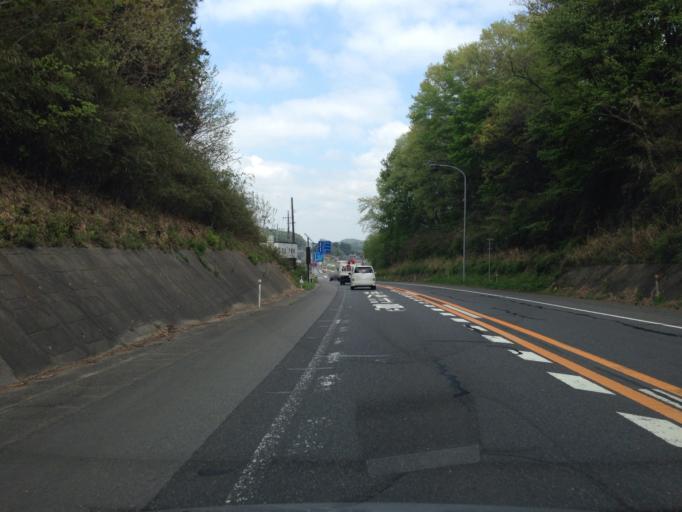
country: JP
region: Ibaraki
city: Iwase
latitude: 36.3493
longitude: 140.1732
